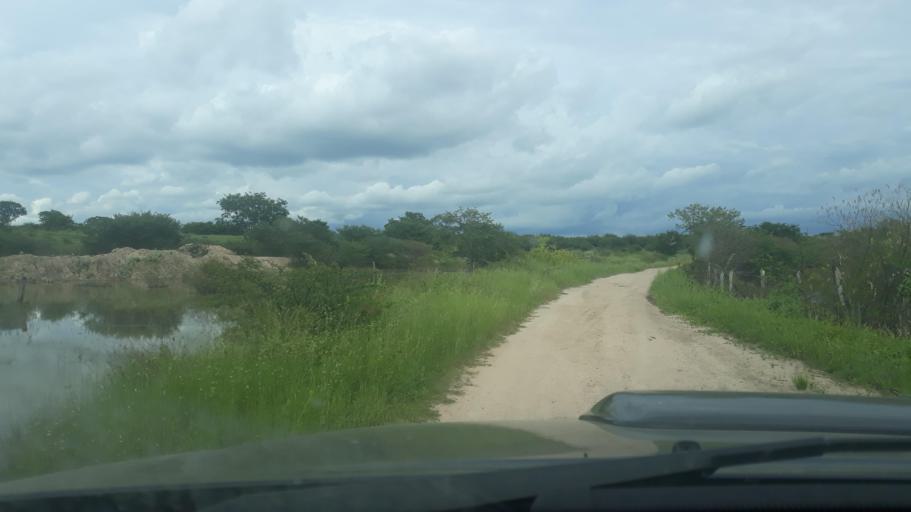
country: BR
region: Bahia
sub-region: Riacho De Santana
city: Riacho de Santana
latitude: -13.8545
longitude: -43.0574
